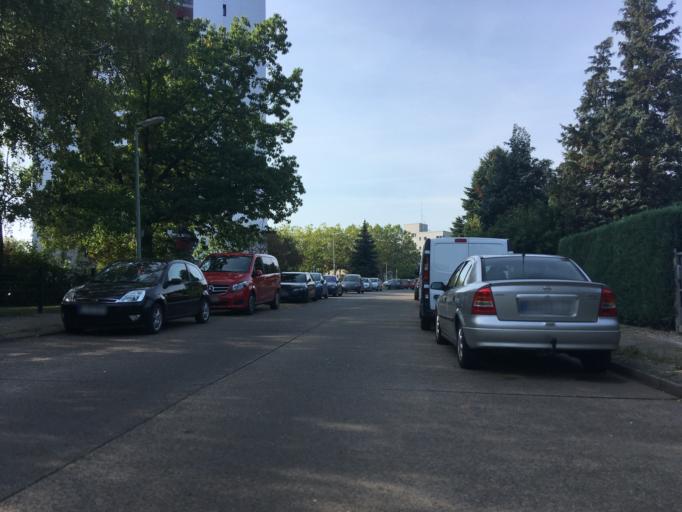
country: DE
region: Berlin
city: Buckow
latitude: 52.4284
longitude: 13.4473
